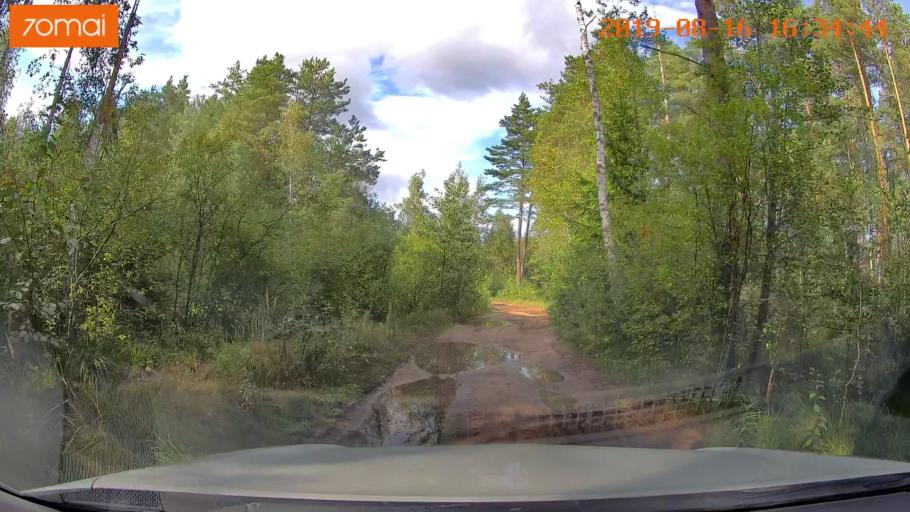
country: BY
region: Mogilev
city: Asipovichy
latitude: 53.2296
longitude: 28.7753
